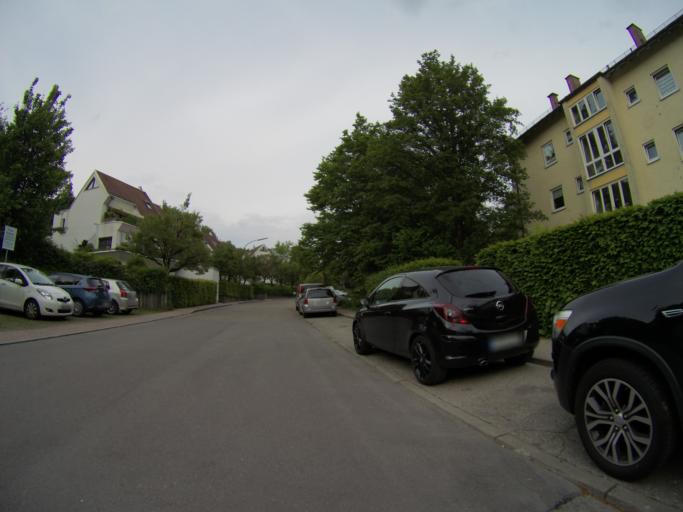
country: DE
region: Bavaria
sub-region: Upper Bavaria
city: Freising
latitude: 48.4130
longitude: 11.7375
